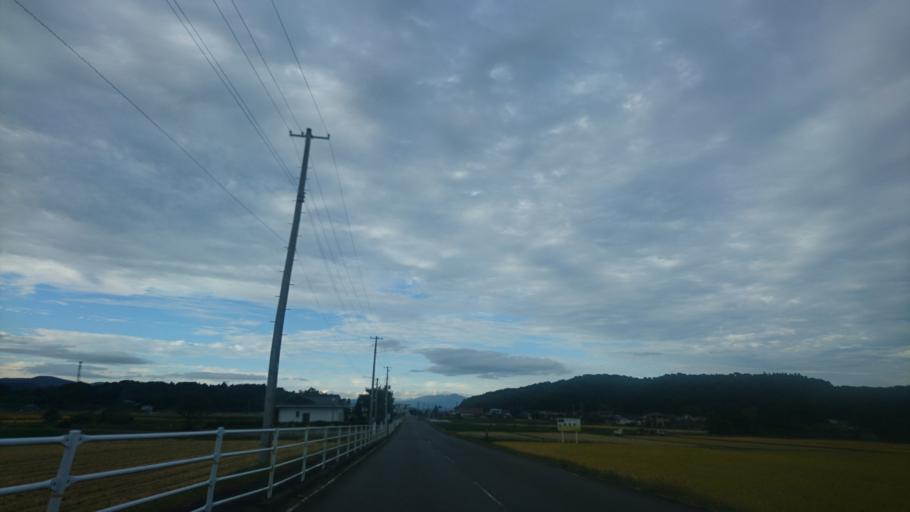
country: JP
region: Fukushima
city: Sukagawa
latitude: 37.3235
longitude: 140.2671
